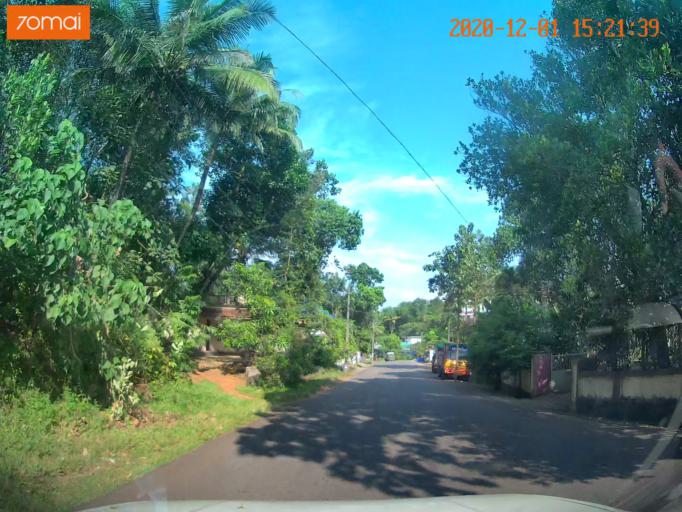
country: IN
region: Kerala
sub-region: Ernakulam
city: Muvattupuzha
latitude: 9.9461
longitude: 76.5438
